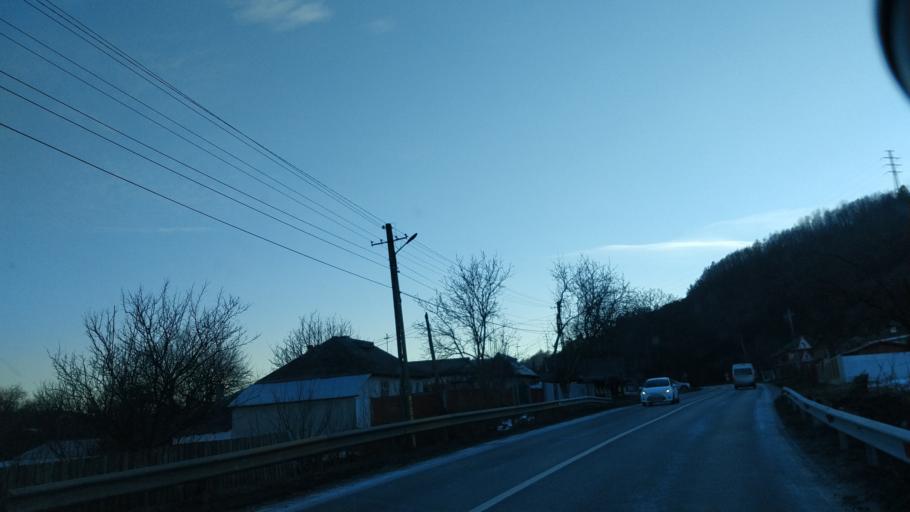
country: RO
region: Bacau
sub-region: Comuna Helegiu
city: Bratila
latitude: 46.3141
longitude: 26.7507
